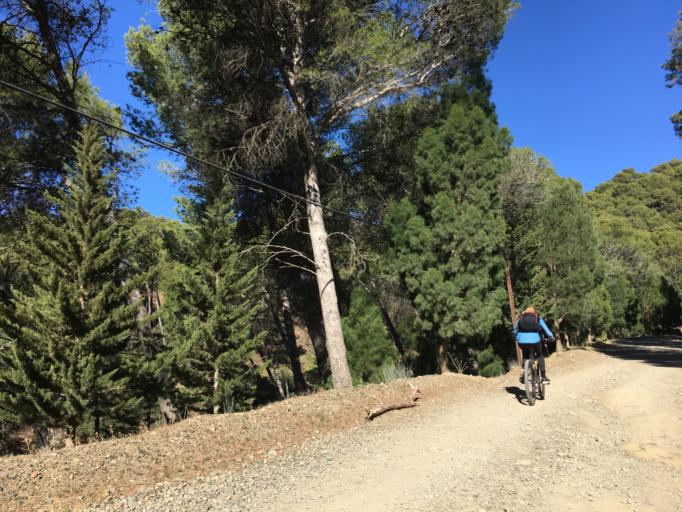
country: ES
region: Andalusia
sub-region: Provincia de Malaga
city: Malaga
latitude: 36.7790
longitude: -4.3852
